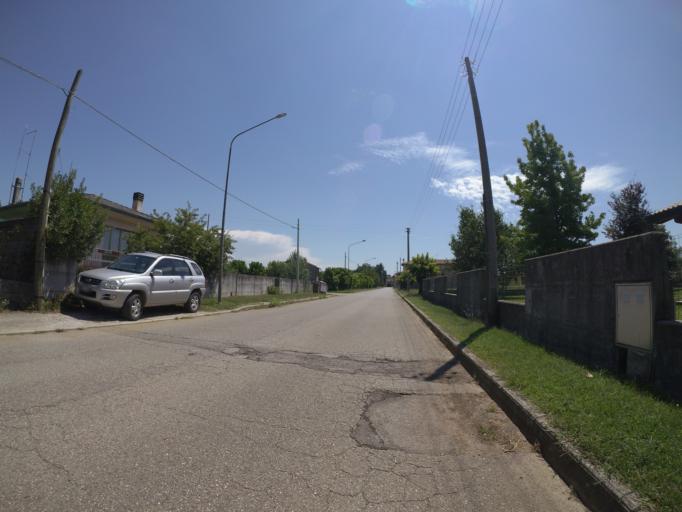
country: IT
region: Friuli Venezia Giulia
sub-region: Provincia di Udine
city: Talmassons
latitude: 45.9327
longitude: 13.1170
